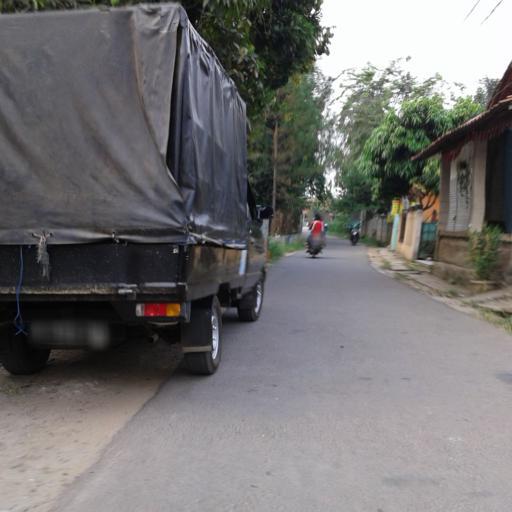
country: ID
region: West Java
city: Sawangan
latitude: -6.4001
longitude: 106.7659
